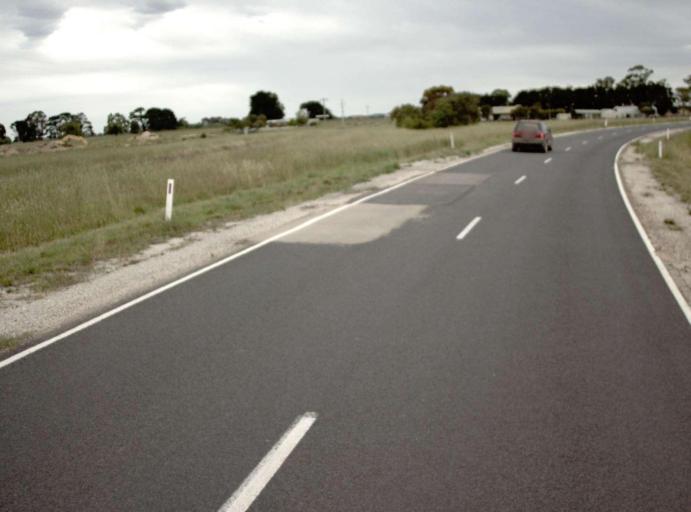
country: AU
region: Victoria
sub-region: Wellington
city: Sale
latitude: -38.0737
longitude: 147.1449
